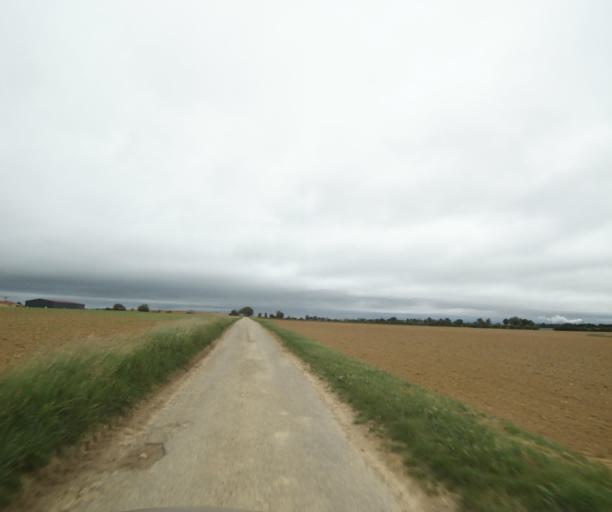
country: FR
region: Rhone-Alpes
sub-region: Departement de l'Ain
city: Miribel
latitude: 45.8362
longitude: 4.9344
